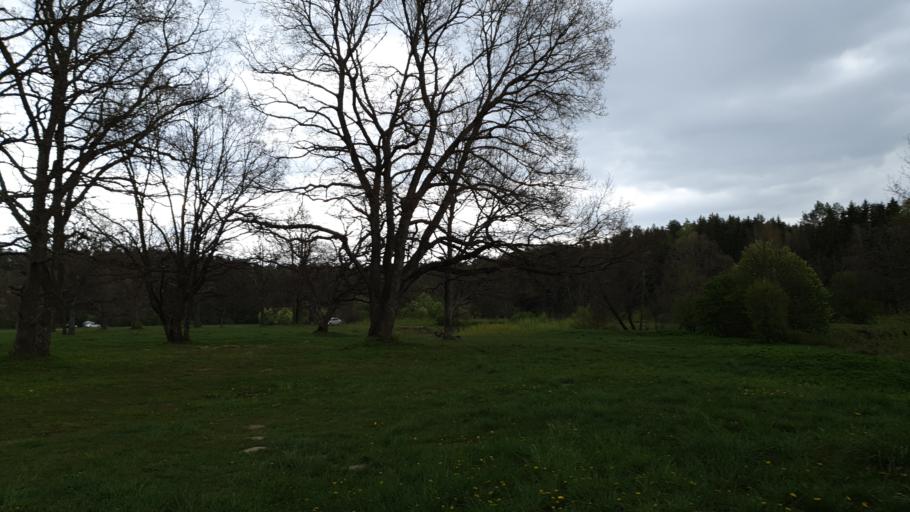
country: BY
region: Minsk
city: Rakaw
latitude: 53.9805
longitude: 26.9722
